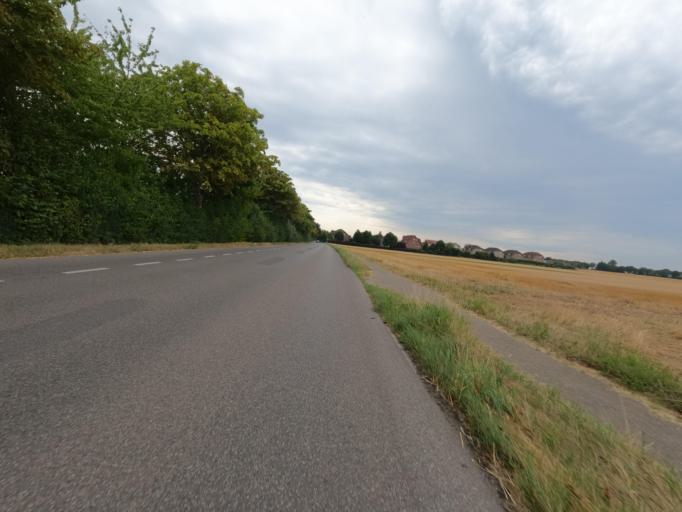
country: DE
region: North Rhine-Westphalia
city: Geilenkirchen
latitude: 50.9758
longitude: 6.1044
